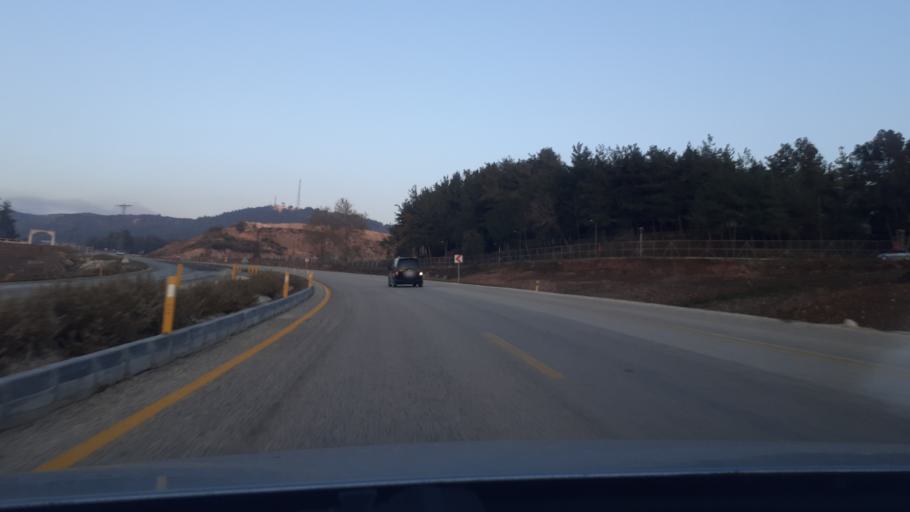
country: TR
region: Hatay
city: Yayladagi
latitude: 35.8911
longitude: 36.0919
